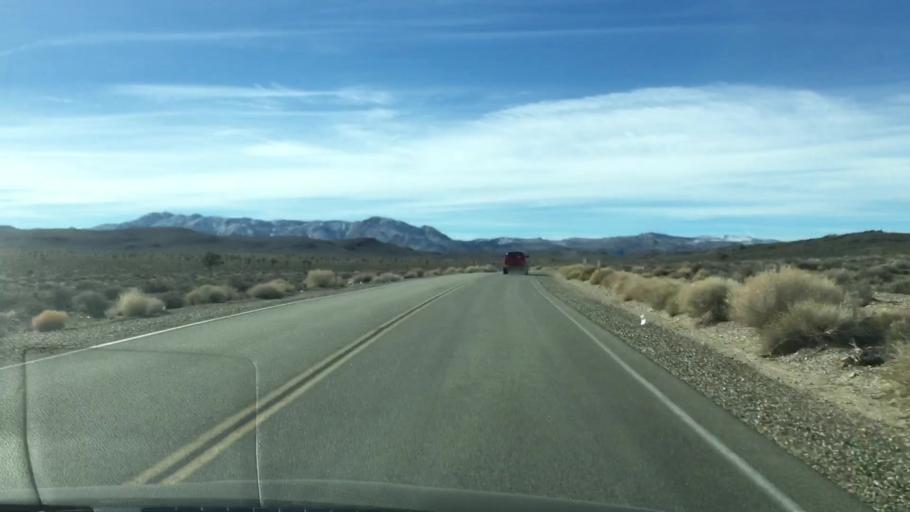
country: US
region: California
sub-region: Inyo County
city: Lone Pine
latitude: 36.3276
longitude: -117.6580
